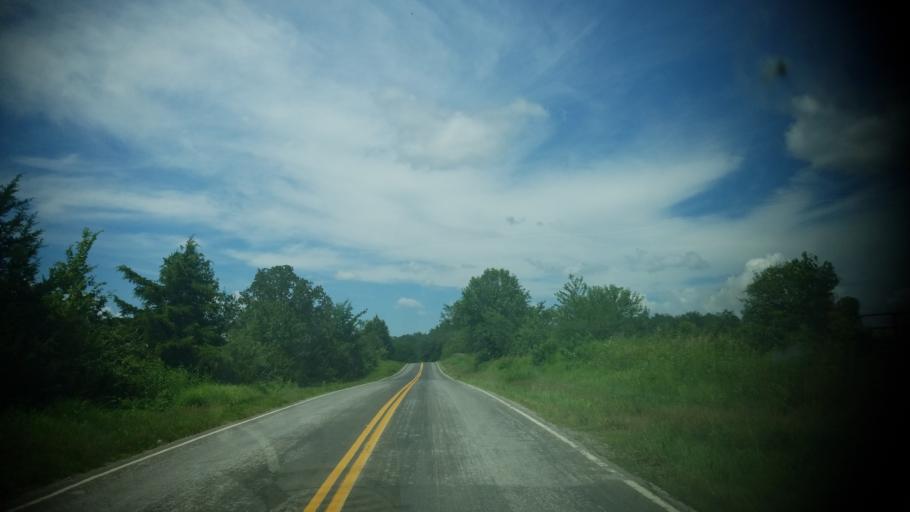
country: US
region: Missouri
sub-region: Audrain County
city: Vandalia
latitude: 39.3136
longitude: -91.3450
